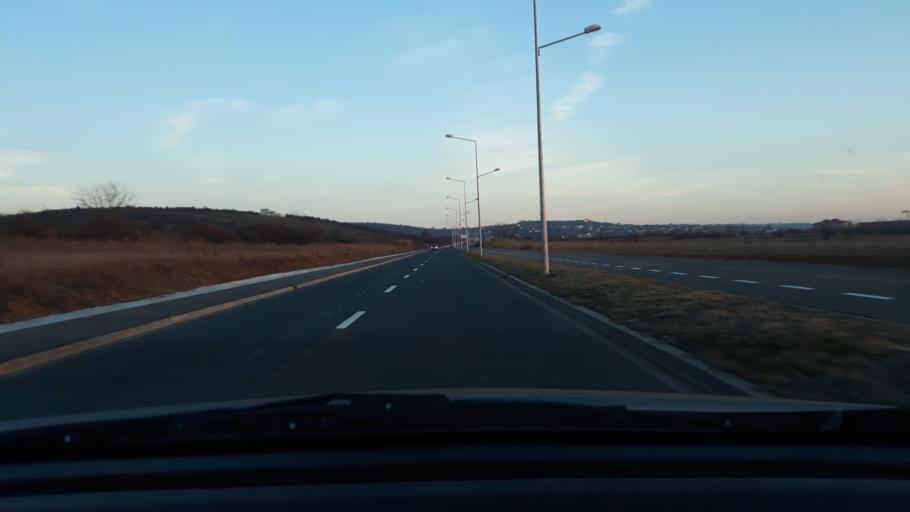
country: RO
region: Bihor
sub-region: Comuna Biharea
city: Oradea
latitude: 47.1016
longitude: 21.9124
